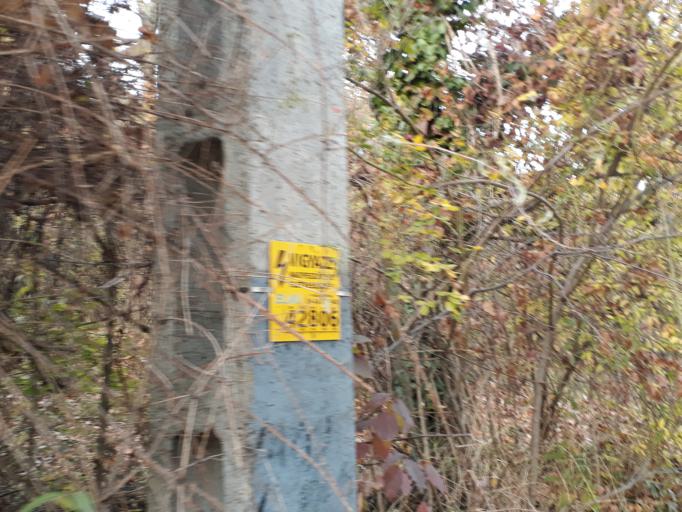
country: HU
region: Pest
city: Budaors
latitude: 47.4758
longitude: 18.9738
